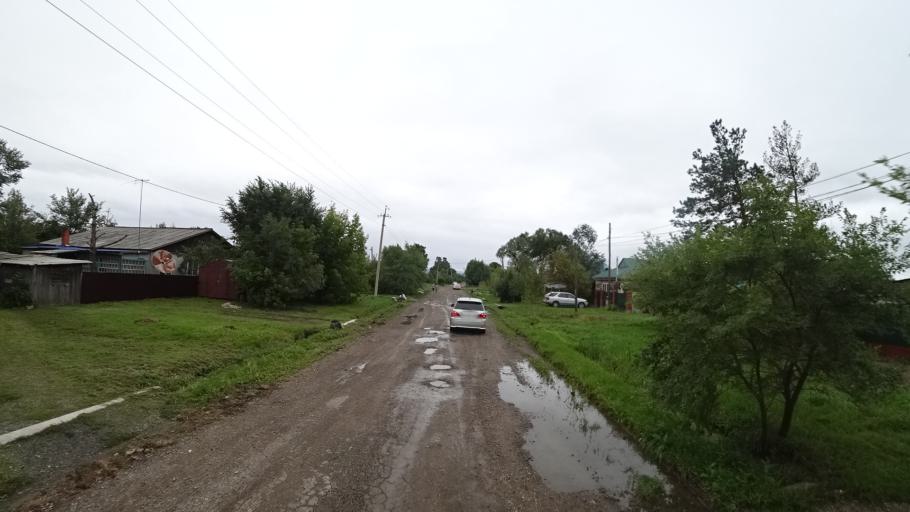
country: RU
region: Primorskiy
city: Chernigovka
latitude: 44.3502
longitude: 132.5724
